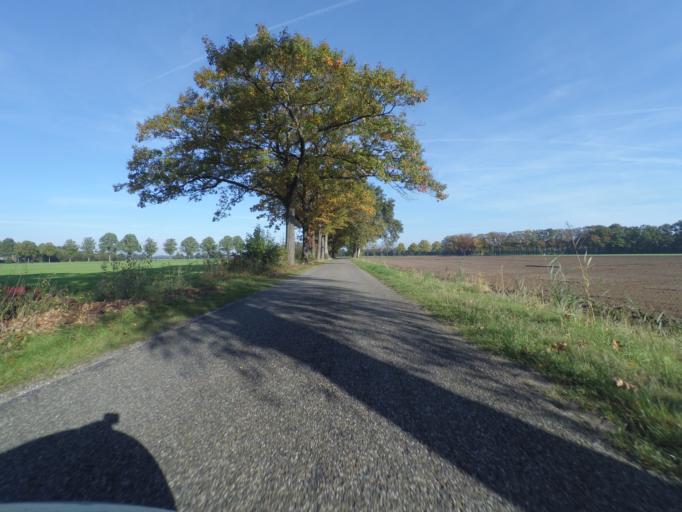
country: NL
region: Gelderland
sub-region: Berkelland
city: Neede
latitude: 52.0797
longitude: 6.5781
